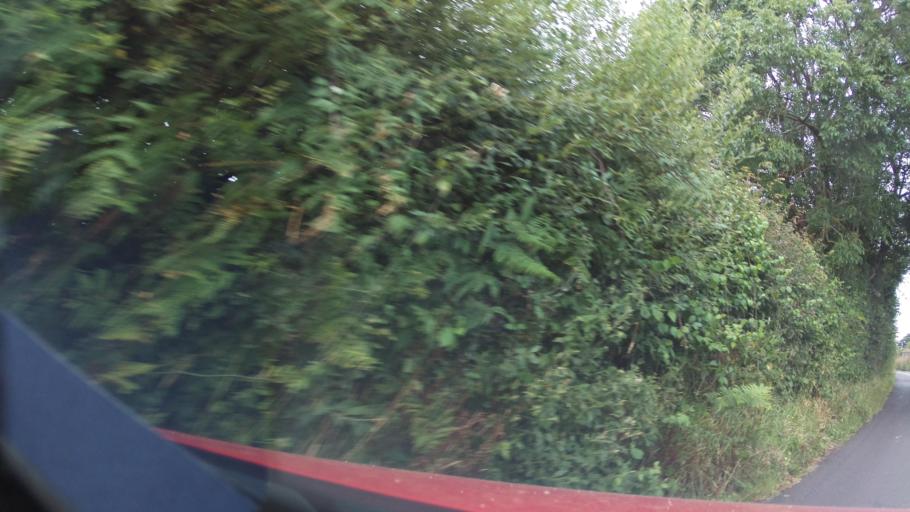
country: GB
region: England
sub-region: Dorset
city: Stalbridge
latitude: 50.9596
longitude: -2.4119
